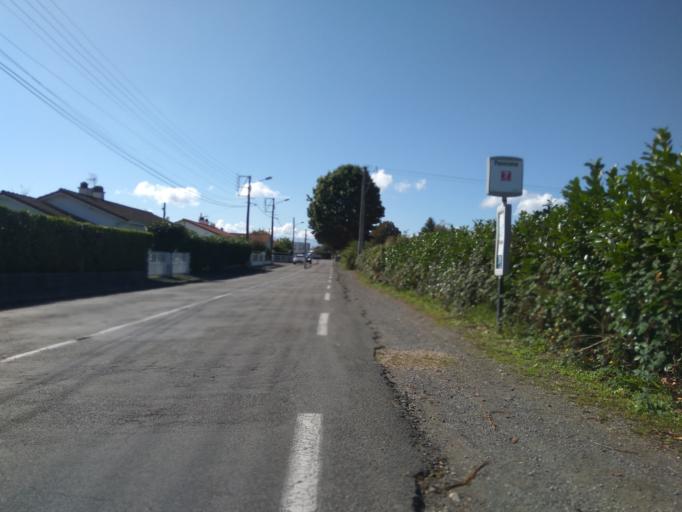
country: FR
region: Aquitaine
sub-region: Departement des Pyrenees-Atlantiques
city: Idron
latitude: 43.3006
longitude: -0.3205
